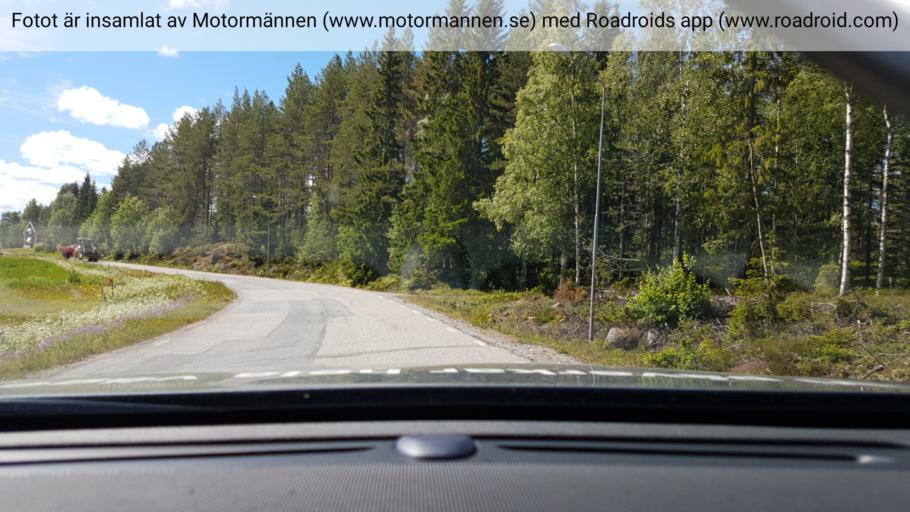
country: SE
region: Vaesterbotten
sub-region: Skelleftea Kommun
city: Burea
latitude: 64.4559
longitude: 21.3587
